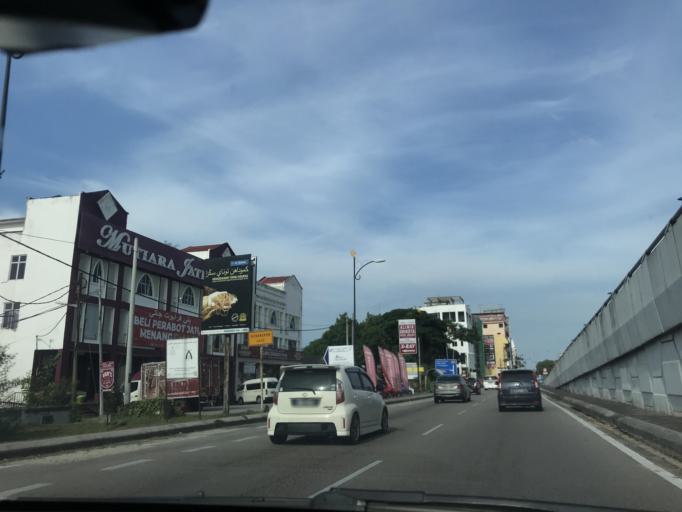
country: MY
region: Kelantan
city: Kota Bharu
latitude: 6.1171
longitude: 102.2445
